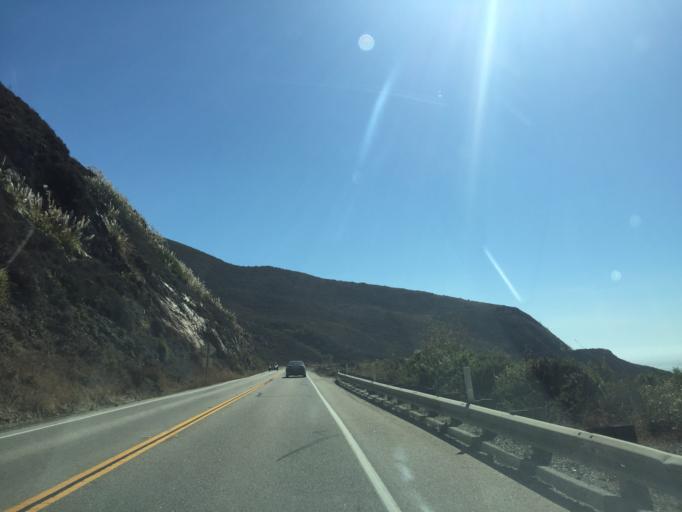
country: US
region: California
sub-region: Monterey County
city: Greenfield
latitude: 36.0542
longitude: -121.5876
